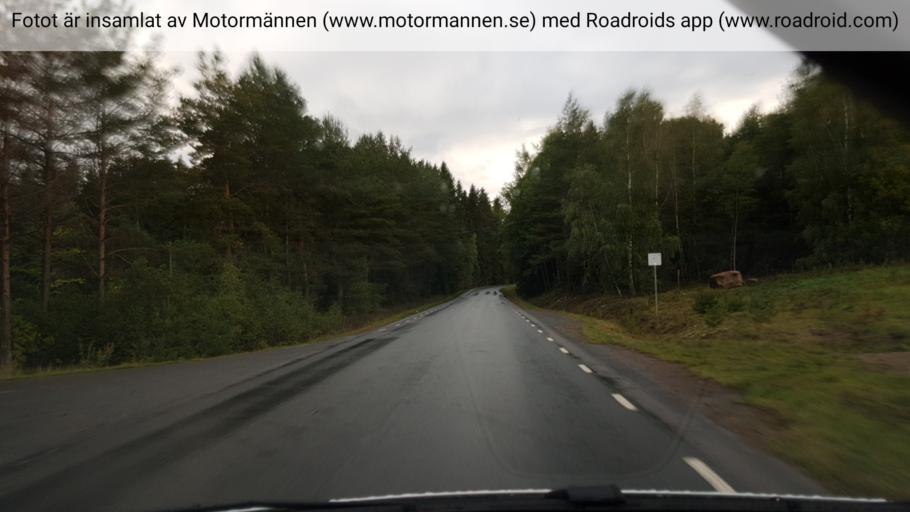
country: SE
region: Vaestra Goetaland
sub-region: Tidaholms Kommun
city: Olofstorp
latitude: 58.3506
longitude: 13.9611
